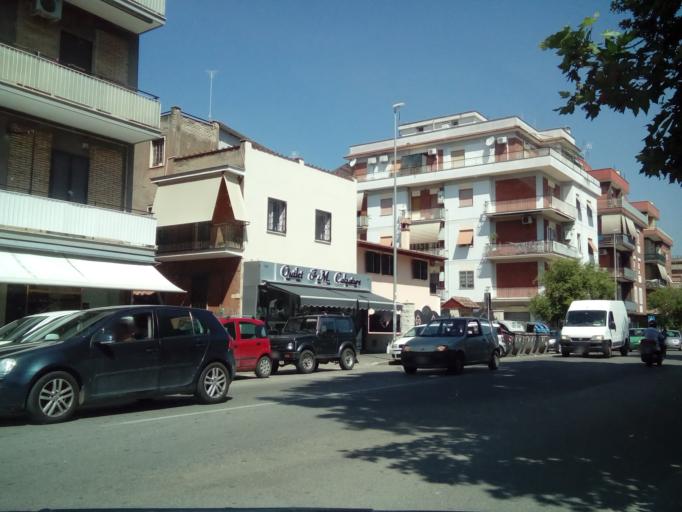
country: IT
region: Latium
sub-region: Citta metropolitana di Roma Capitale
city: Rome
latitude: 41.8774
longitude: 12.5786
